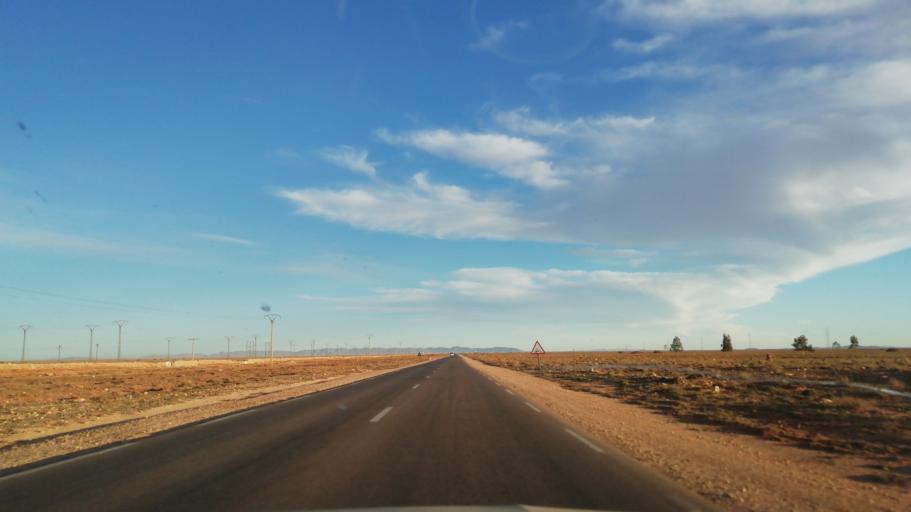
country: DZ
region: Wilaya de Naama
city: Naama
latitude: 33.7436
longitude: -0.7780
